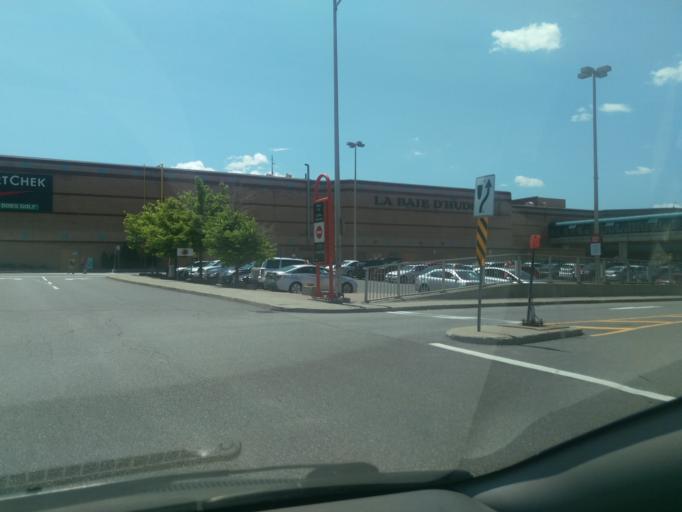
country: CA
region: Quebec
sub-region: Outaouais
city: Gatineau
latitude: 45.4789
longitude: -75.5175
